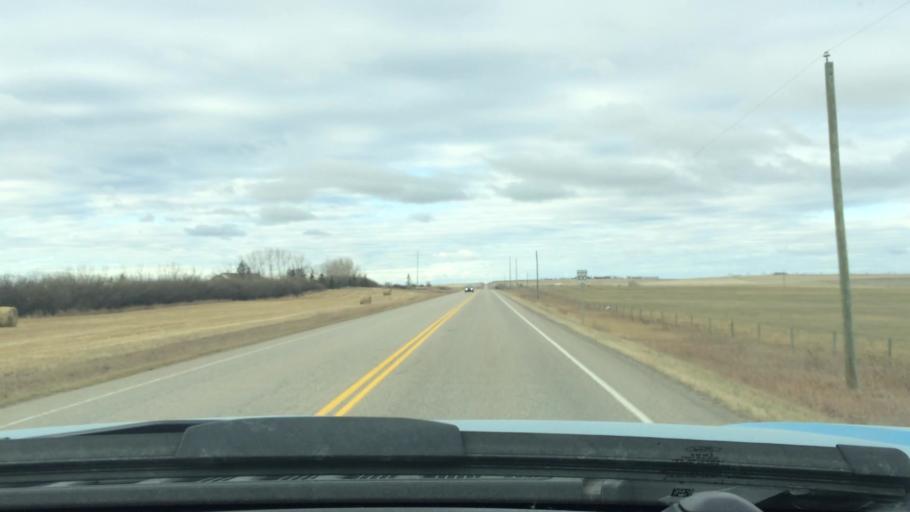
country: CA
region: Alberta
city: Airdrie
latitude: 51.2125
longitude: -114.0738
